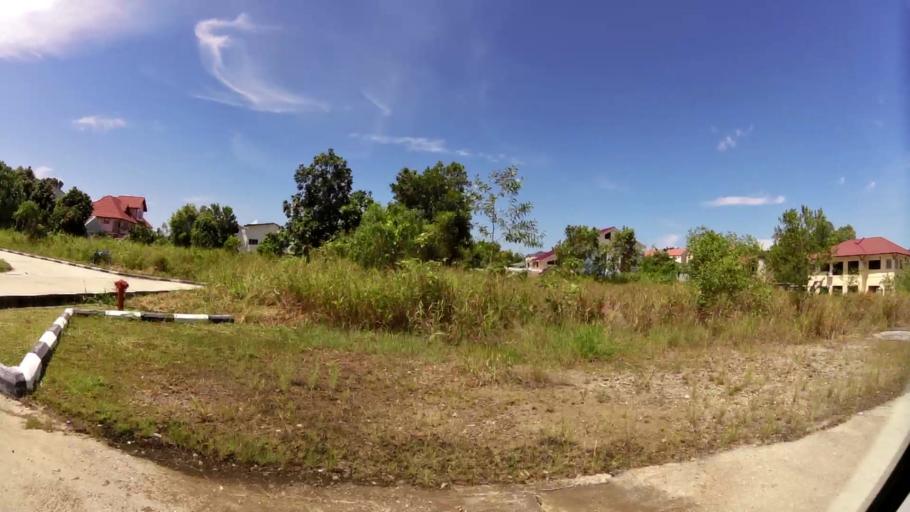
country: BN
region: Brunei and Muara
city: Bandar Seri Begawan
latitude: 4.9345
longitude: 114.9491
